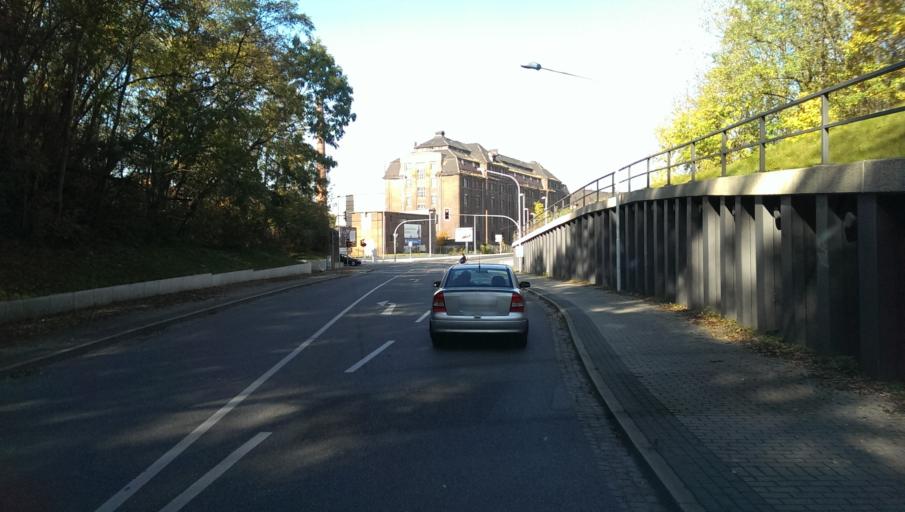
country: DE
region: Saxony
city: Riesa
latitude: 51.3140
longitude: 13.2634
